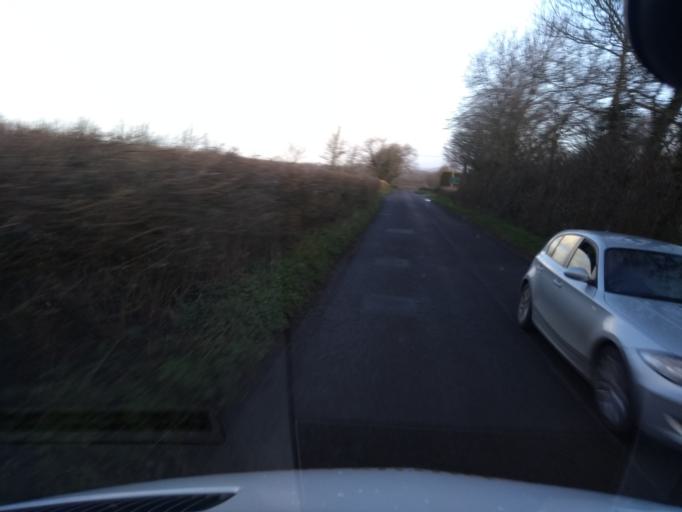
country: GB
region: England
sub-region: Somerset
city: Wedmore
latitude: 51.2359
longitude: -2.8190
